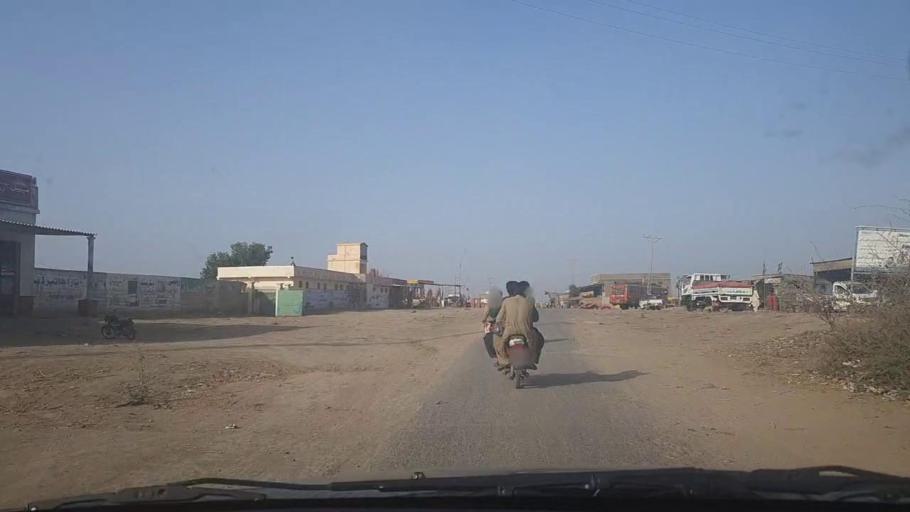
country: PK
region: Sindh
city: Keti Bandar
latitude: 24.3134
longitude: 67.6122
